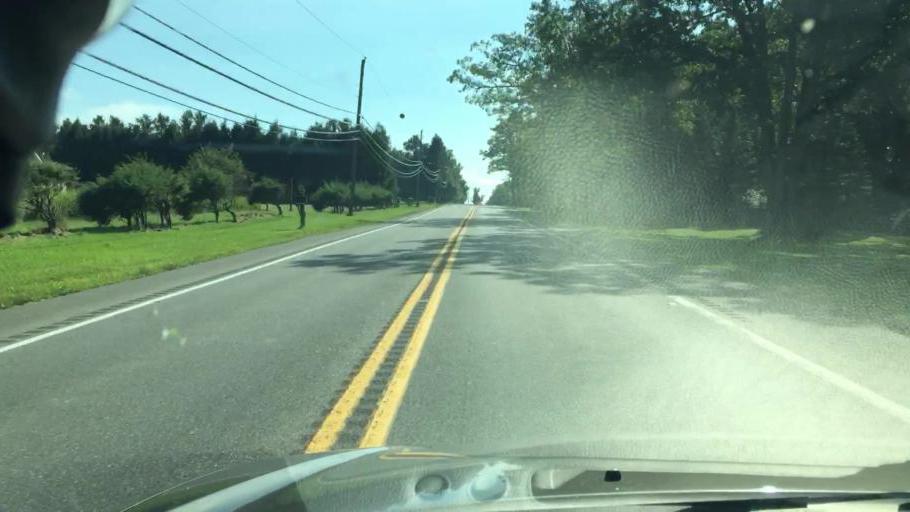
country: US
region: Pennsylvania
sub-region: Carbon County
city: Jim Thorpe
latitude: 40.9067
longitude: -75.6791
